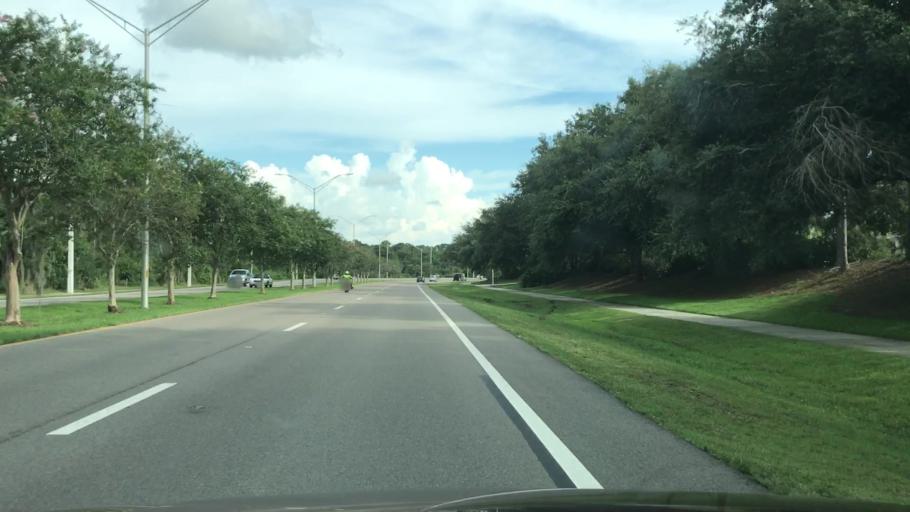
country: US
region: Florida
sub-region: Sarasota County
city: Venice Gardens
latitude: 27.0873
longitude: -82.3887
